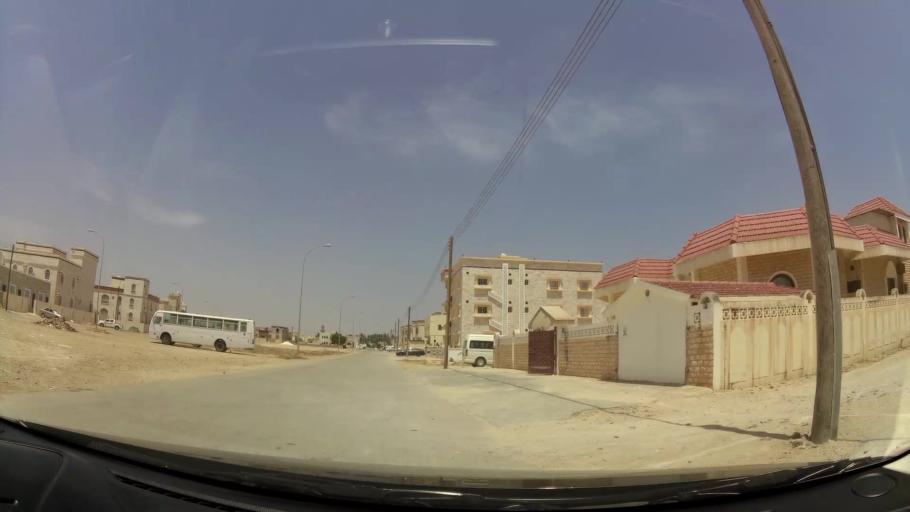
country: OM
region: Zufar
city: Salalah
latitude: 17.0675
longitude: 54.1486
